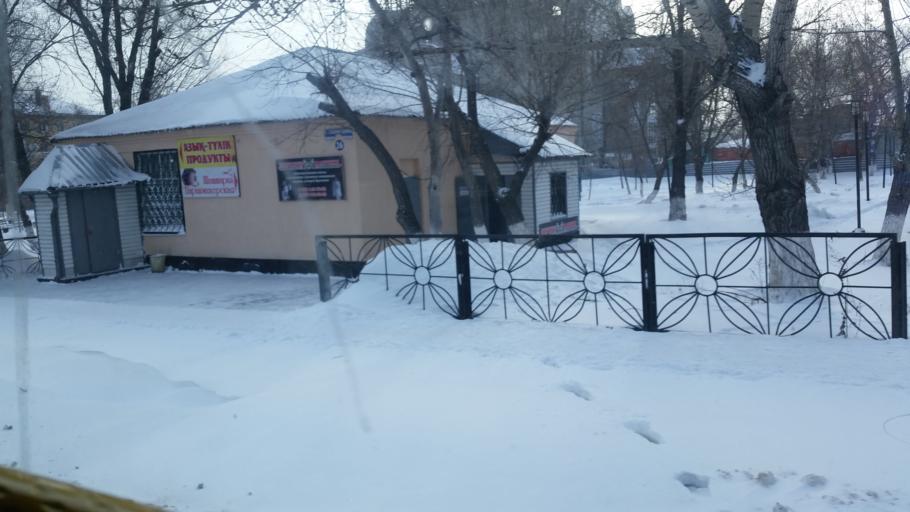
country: KZ
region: Qaraghandy
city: Aqtas
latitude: 49.8077
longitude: 73.0553
